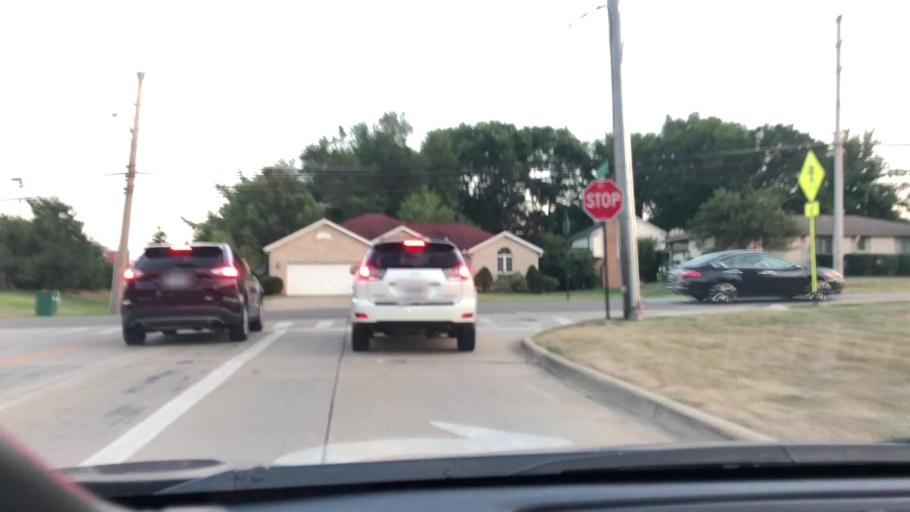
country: US
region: Ohio
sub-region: Summit County
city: Green
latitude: 40.9595
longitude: -81.4679
